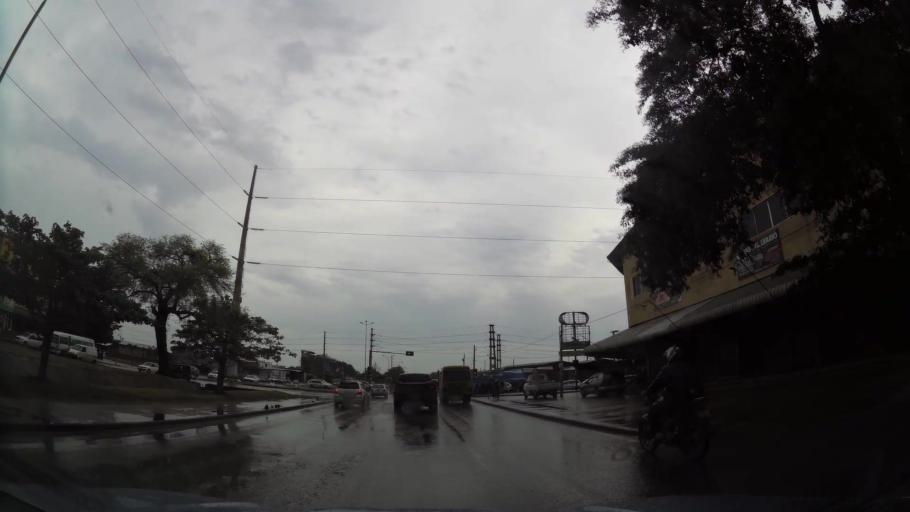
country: BO
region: Santa Cruz
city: Santa Cruz de la Sierra
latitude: -17.7883
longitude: -63.1484
